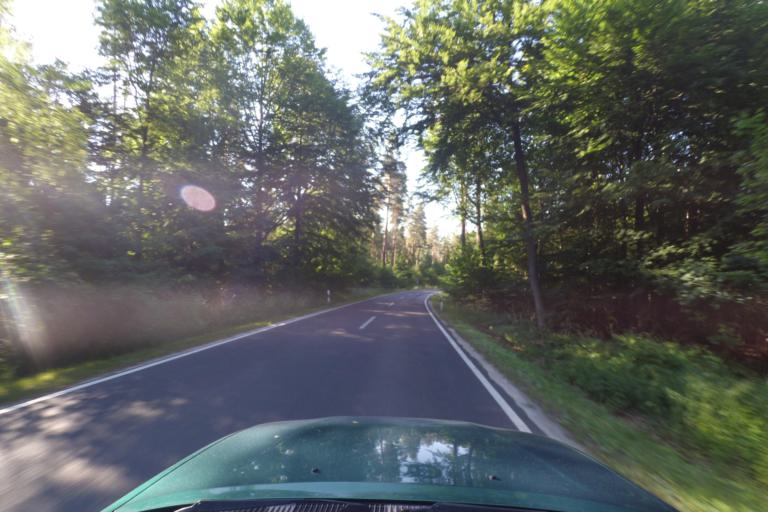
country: DE
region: Bavaria
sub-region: Upper Palatinate
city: Speinshart
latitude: 49.7946
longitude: 11.8201
